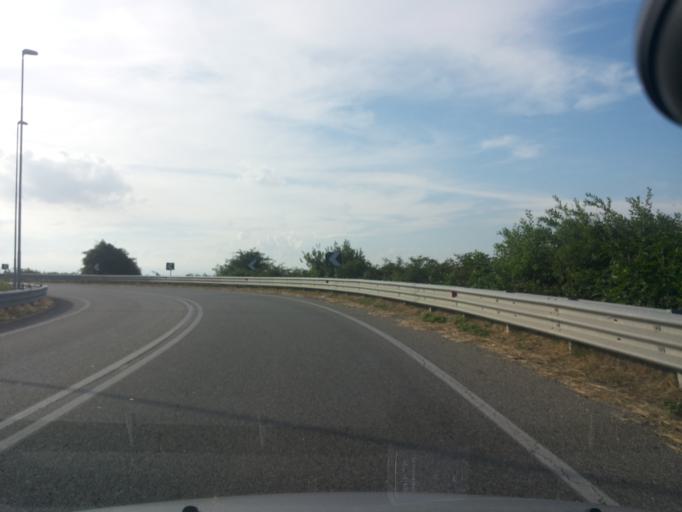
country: IT
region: Piedmont
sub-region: Provincia di Vercelli
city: Borgo Vercelli
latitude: 45.3652
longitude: 8.4627
